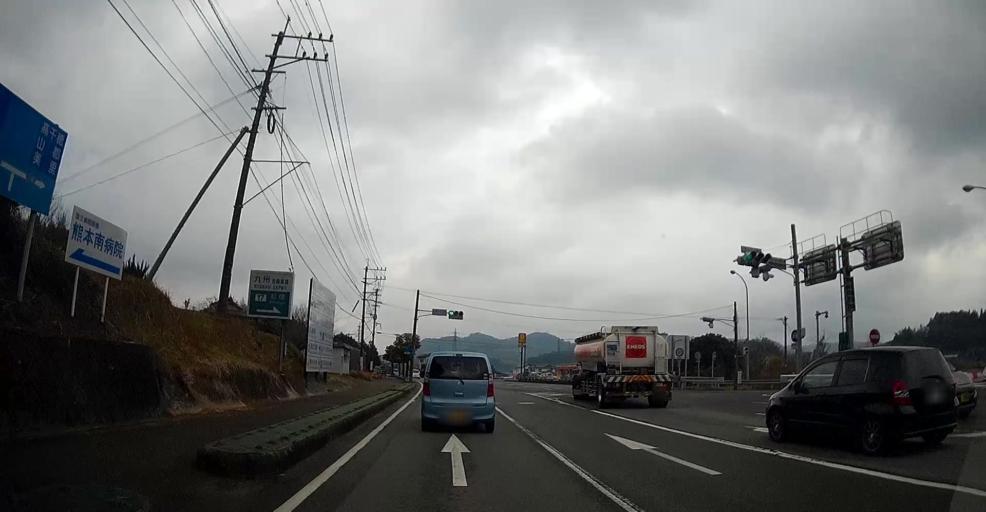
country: JP
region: Kumamoto
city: Matsubase
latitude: 32.6502
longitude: 130.7102
